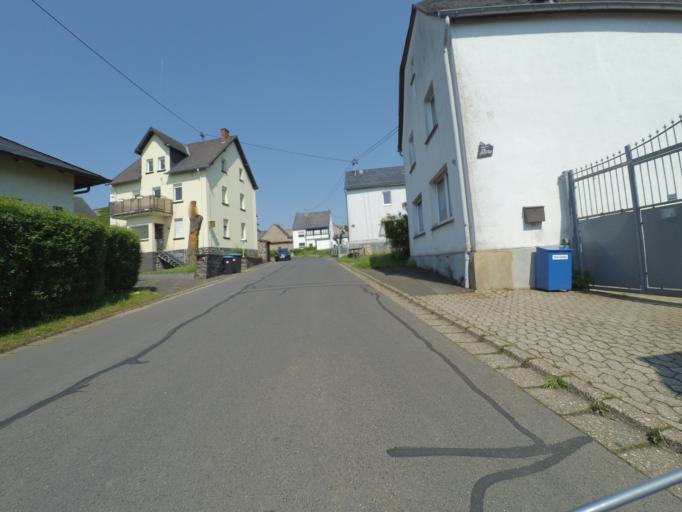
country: DE
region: Rheinland-Pfalz
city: Gering
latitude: 50.2743
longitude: 7.2614
